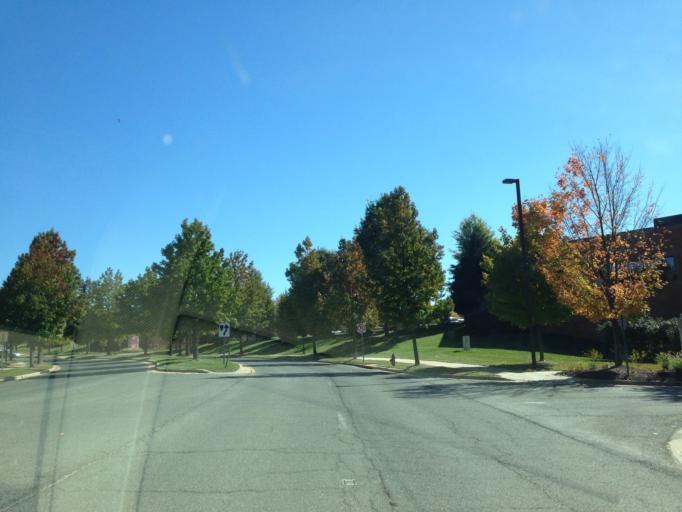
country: US
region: Maryland
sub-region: Montgomery County
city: Germantown
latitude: 39.1901
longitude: -77.2564
